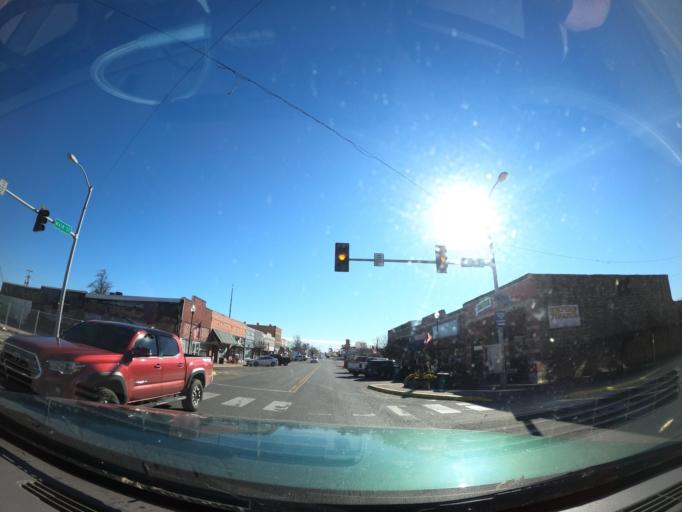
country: US
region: Oklahoma
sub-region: McIntosh County
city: Eufaula
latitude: 35.2866
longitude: -95.5825
